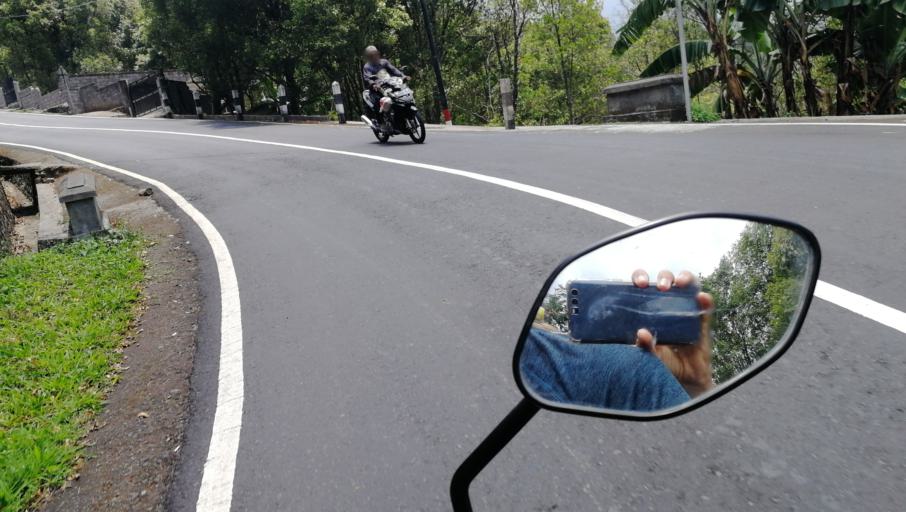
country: ID
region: Bali
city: Munduk
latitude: -8.2604
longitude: 115.0694
